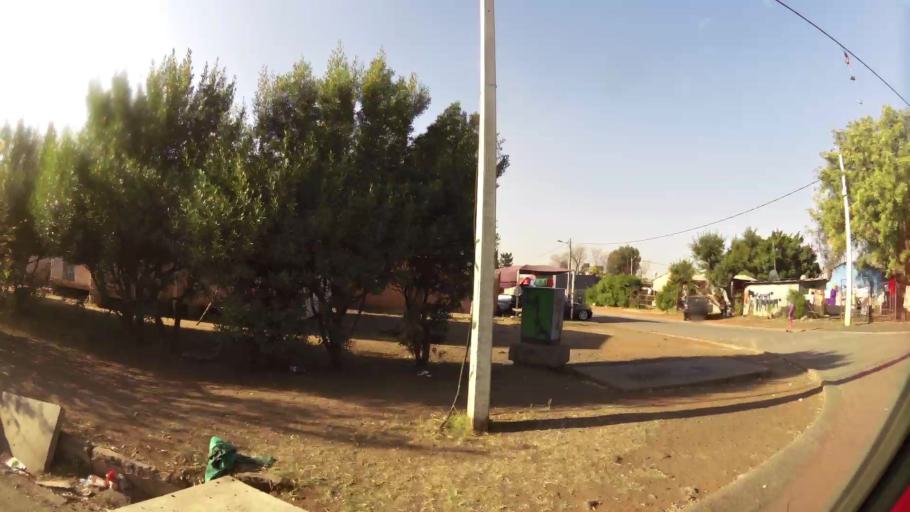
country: ZA
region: North-West
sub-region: Bojanala Platinum District Municipality
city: Rustenburg
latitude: -25.6434
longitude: 27.2379
